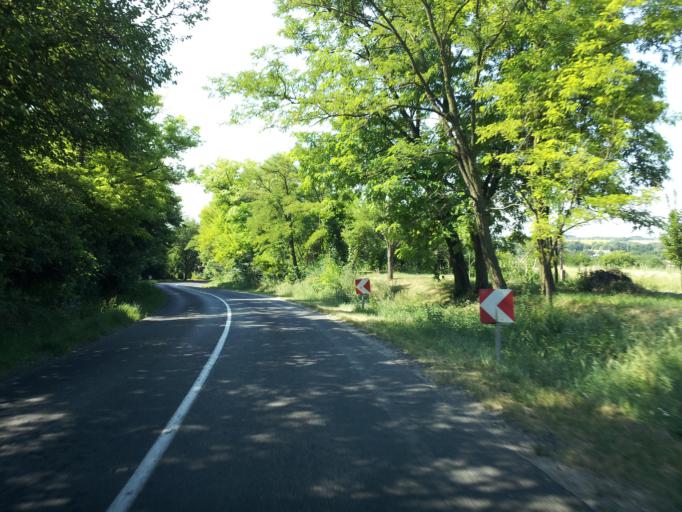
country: HU
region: Fejer
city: Lovasbereny
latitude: 47.3774
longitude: 18.5815
